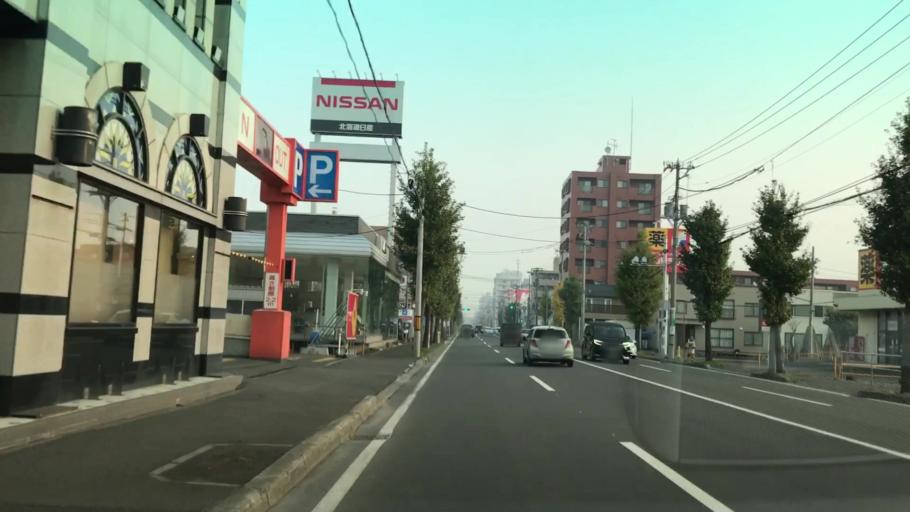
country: JP
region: Hokkaido
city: Sapporo
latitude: 43.1035
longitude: 141.3297
